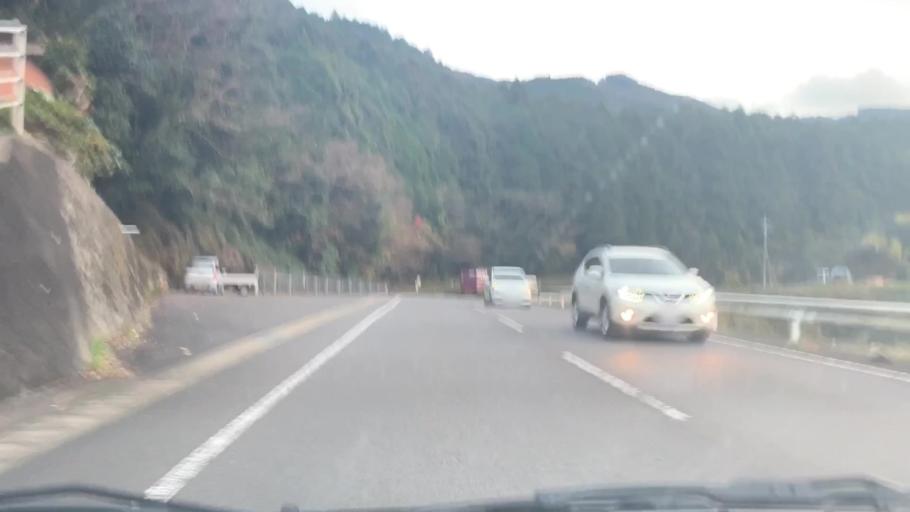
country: JP
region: Saga Prefecture
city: Kashima
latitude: 33.0205
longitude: 130.0674
